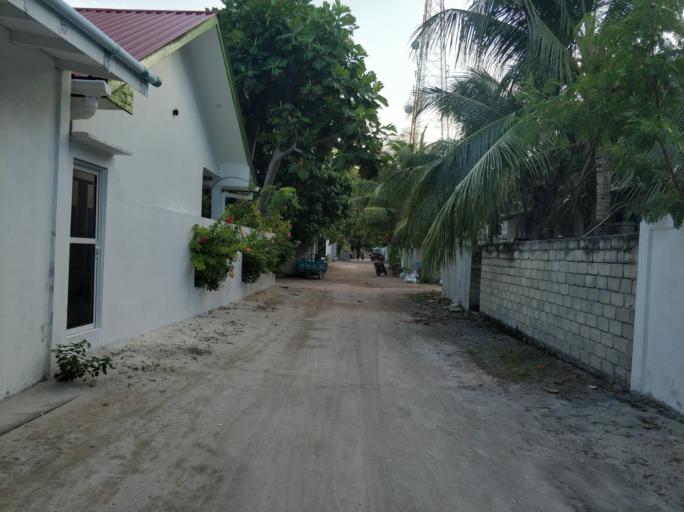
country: MV
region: Maale
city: Male
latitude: 4.4398
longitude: 72.9614
